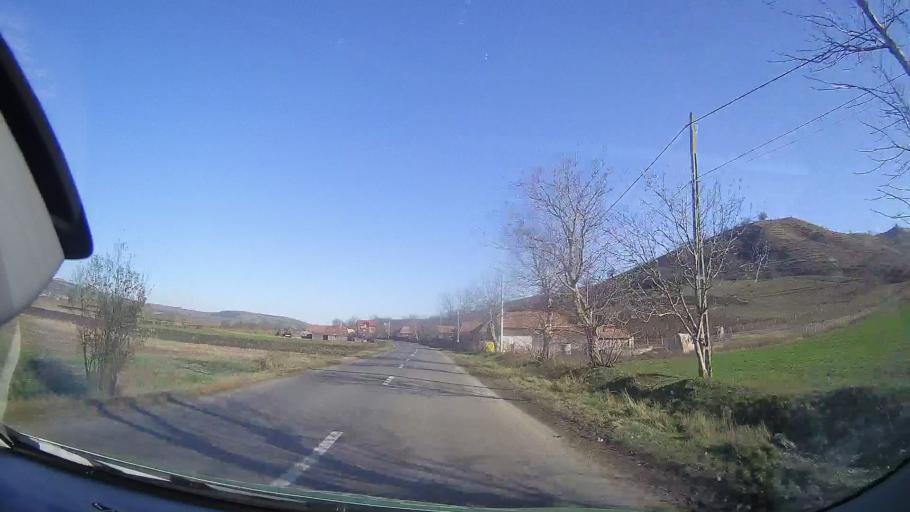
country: RO
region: Mures
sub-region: Comuna Band
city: Band
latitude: 46.5632
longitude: 24.3382
